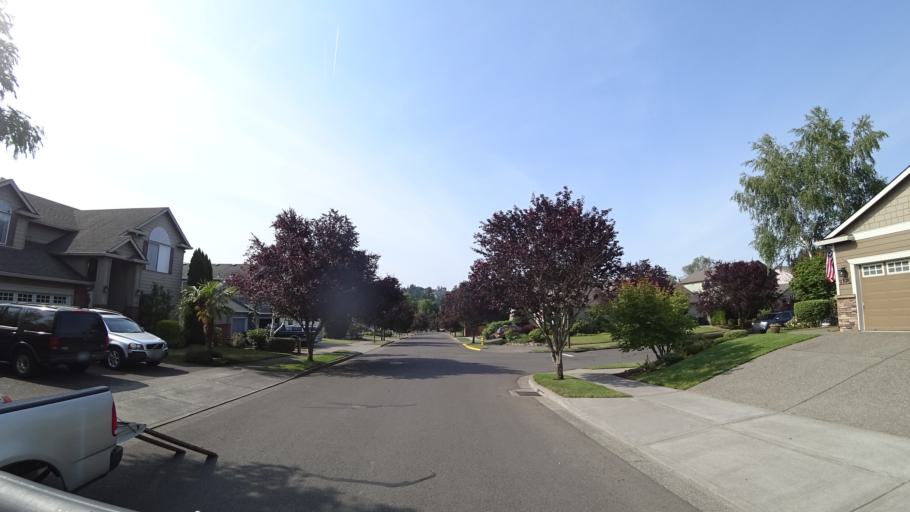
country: US
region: Oregon
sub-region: Clackamas County
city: Happy Valley
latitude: 45.4522
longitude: -122.5235
